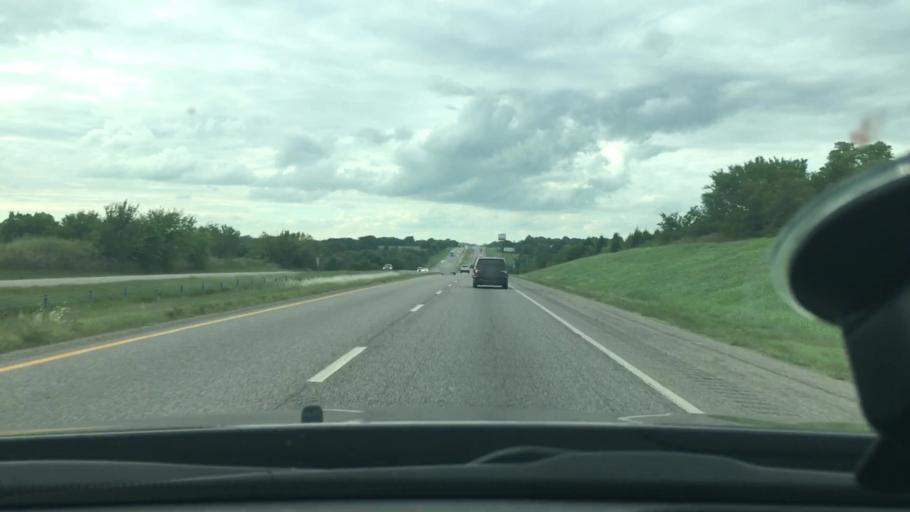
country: US
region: Oklahoma
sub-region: Cleveland County
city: Noble
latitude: 35.0993
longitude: -97.4268
